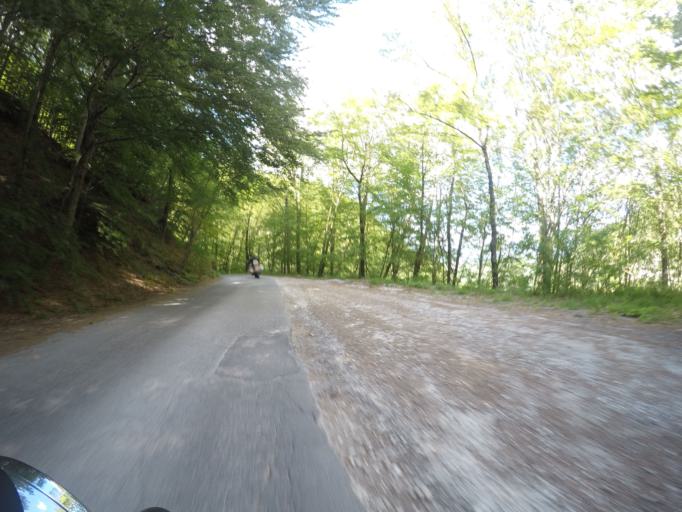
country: IT
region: Tuscany
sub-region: Provincia di Lucca
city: Minucciano
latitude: 44.1478
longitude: 10.1950
